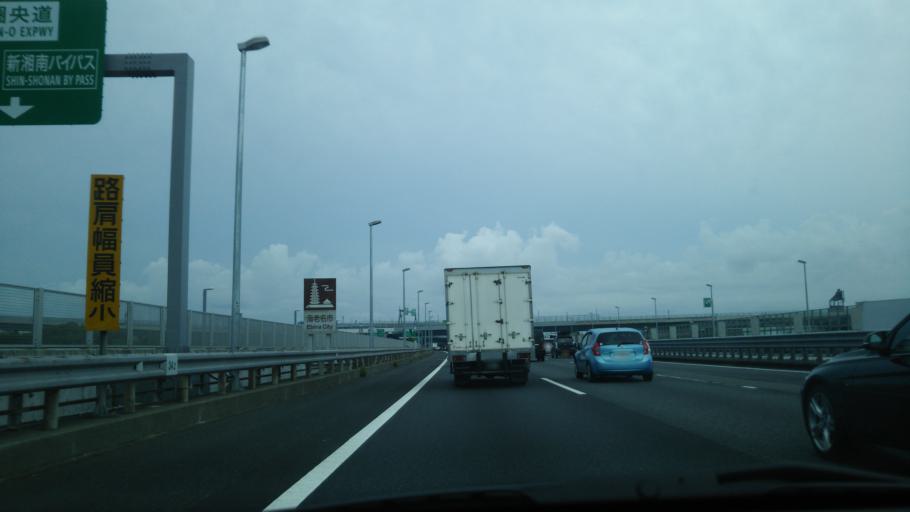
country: JP
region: Kanagawa
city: Atsugi
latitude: 35.4228
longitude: 139.3715
